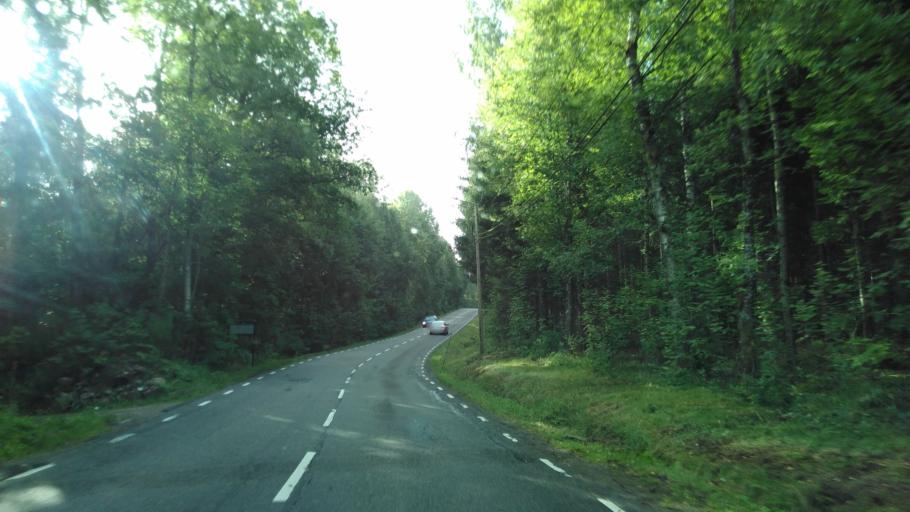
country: SE
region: Vaestra Goetaland
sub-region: Boras Kommun
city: Ganghester
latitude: 57.7920
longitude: 13.0150
